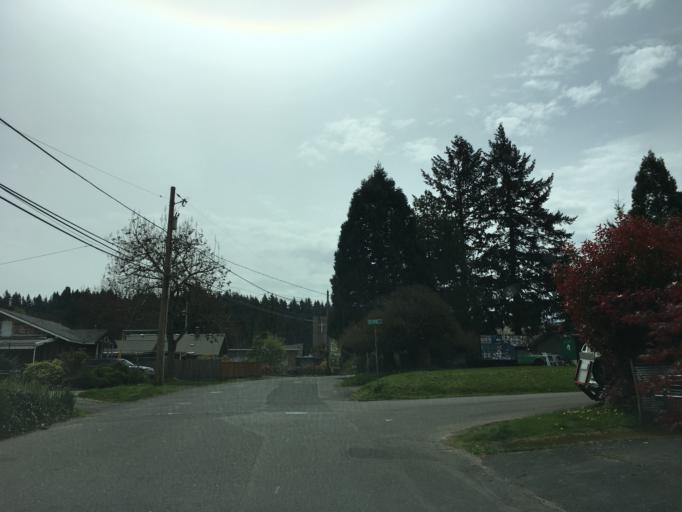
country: US
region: Oregon
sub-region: Multnomah County
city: Lents
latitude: 45.5576
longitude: -122.5734
